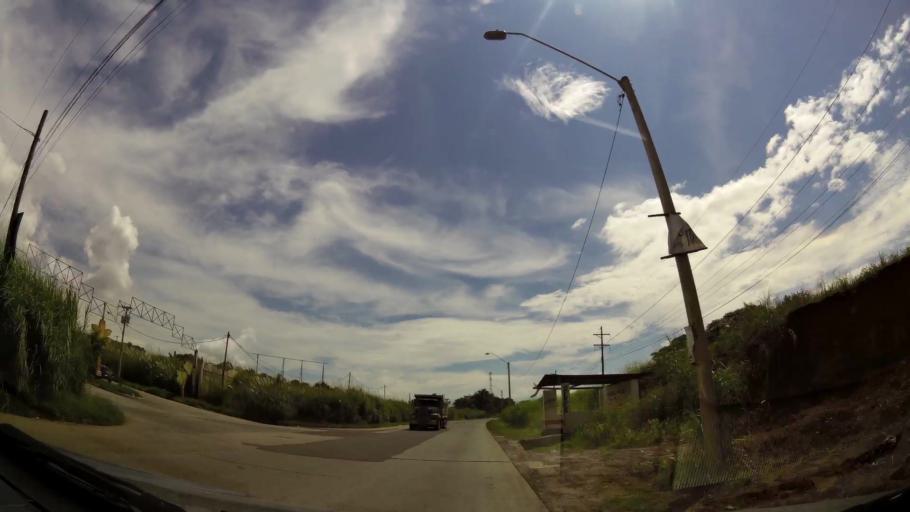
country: PA
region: Panama
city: San Vicente de Bique
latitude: 8.9170
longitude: -79.6933
